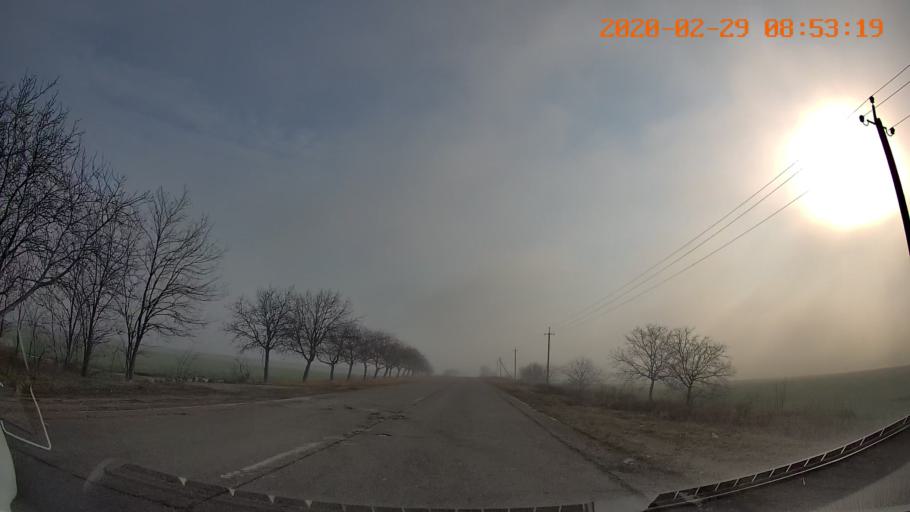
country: MD
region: Telenesti
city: Tiraspolul Nou
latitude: 46.9255
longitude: 29.5545
